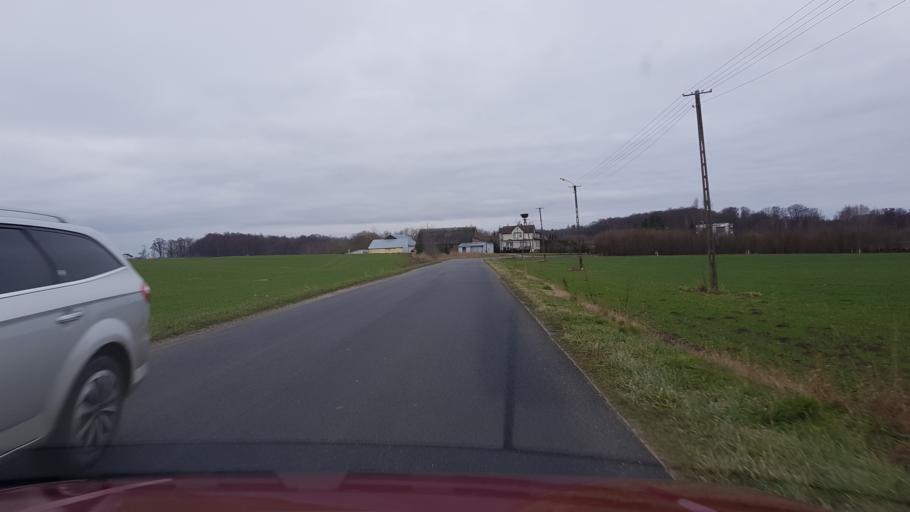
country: PL
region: West Pomeranian Voivodeship
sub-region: Powiat koszalinski
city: Mielno
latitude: 54.1756
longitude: 16.0085
